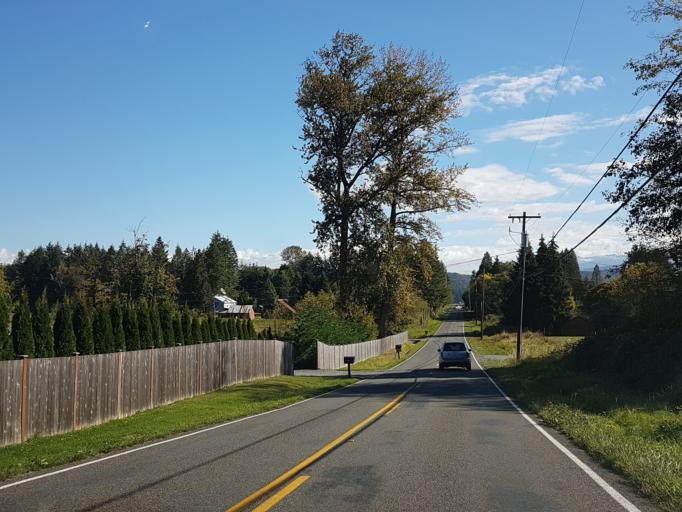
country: US
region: Washington
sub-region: Snohomish County
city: Cathcart
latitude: 47.8484
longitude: -122.1150
